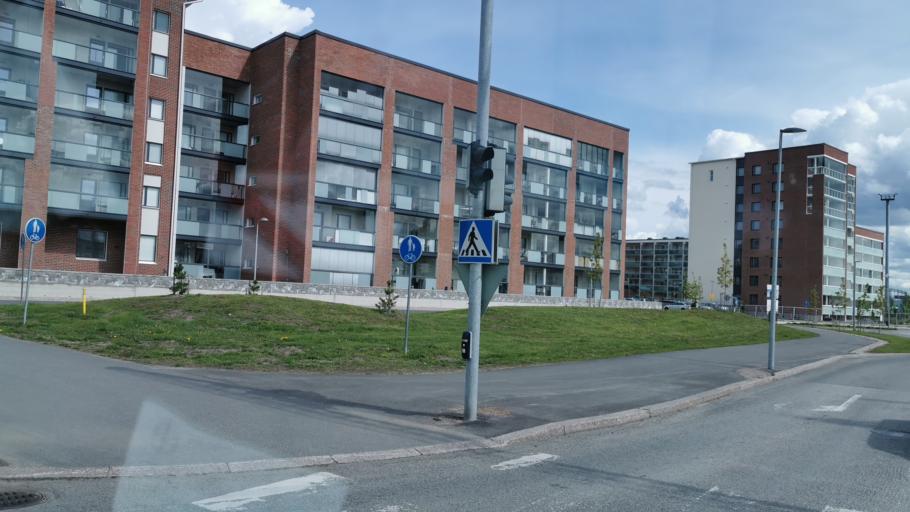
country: FI
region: Northern Ostrobothnia
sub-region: Oulu
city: Oulu
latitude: 64.9989
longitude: 25.4645
